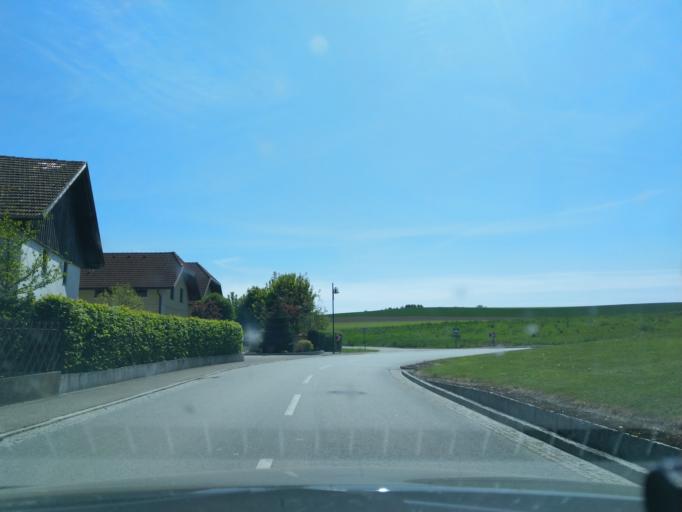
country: DE
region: Bavaria
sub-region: Lower Bavaria
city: Bad Fussing
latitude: 48.2759
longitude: 13.3669
